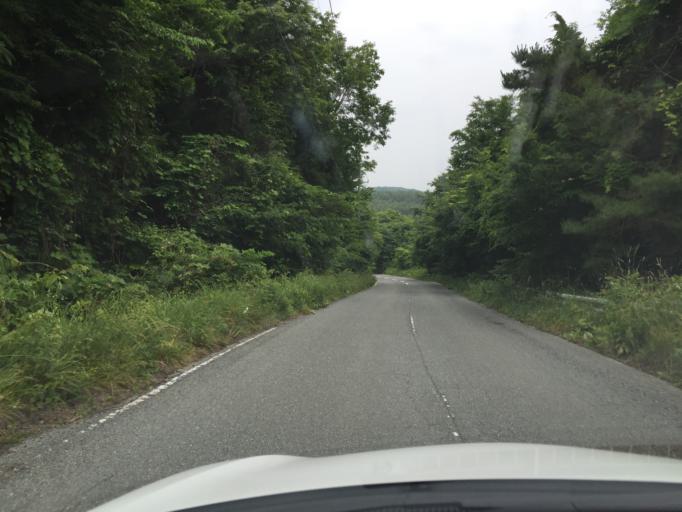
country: JP
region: Fukushima
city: Iwaki
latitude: 37.1602
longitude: 140.7030
